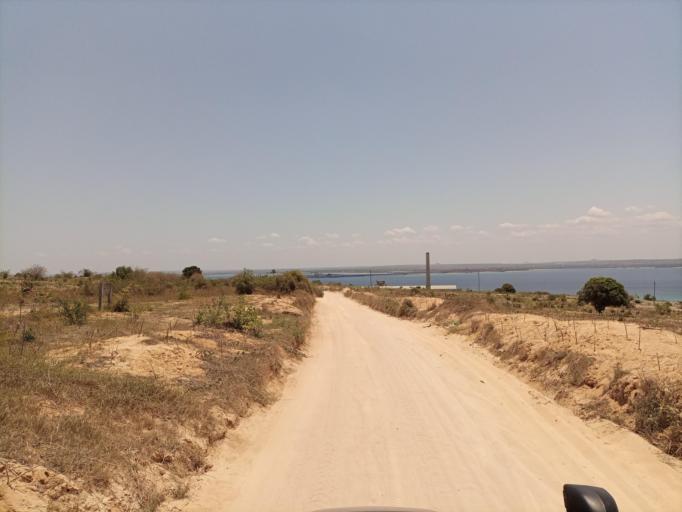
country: MZ
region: Nampula
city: Nacala
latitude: -14.5178
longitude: 40.6820
